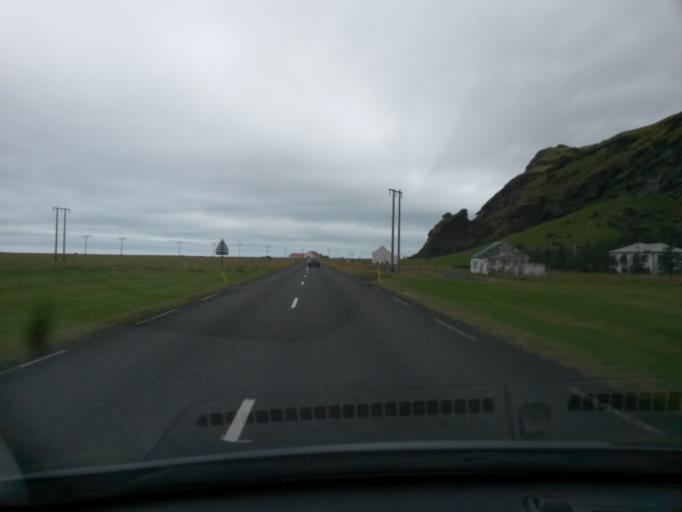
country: IS
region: South
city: Vestmannaeyjar
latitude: 63.5229
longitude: -19.5652
